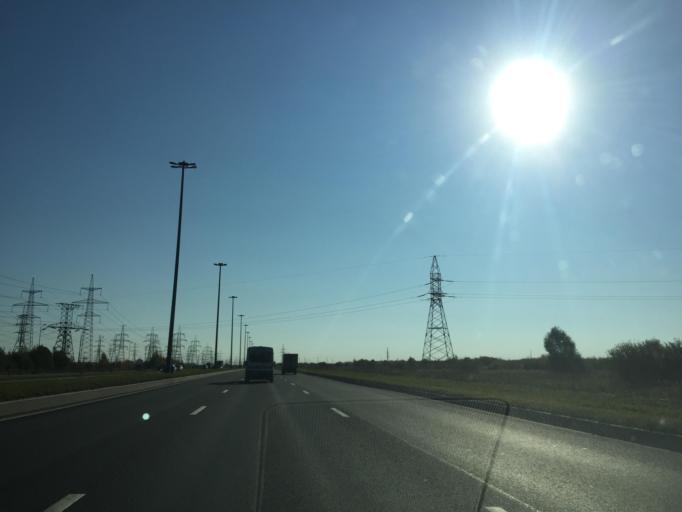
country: RU
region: St.-Petersburg
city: Petro-Slavyanka
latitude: 59.7593
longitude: 30.5136
